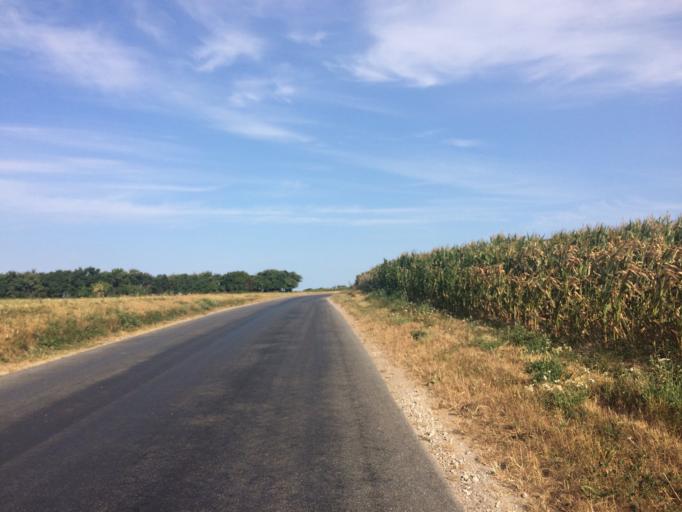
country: DK
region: Central Jutland
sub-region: Holstebro Kommune
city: Vinderup
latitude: 56.5667
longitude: 8.7584
